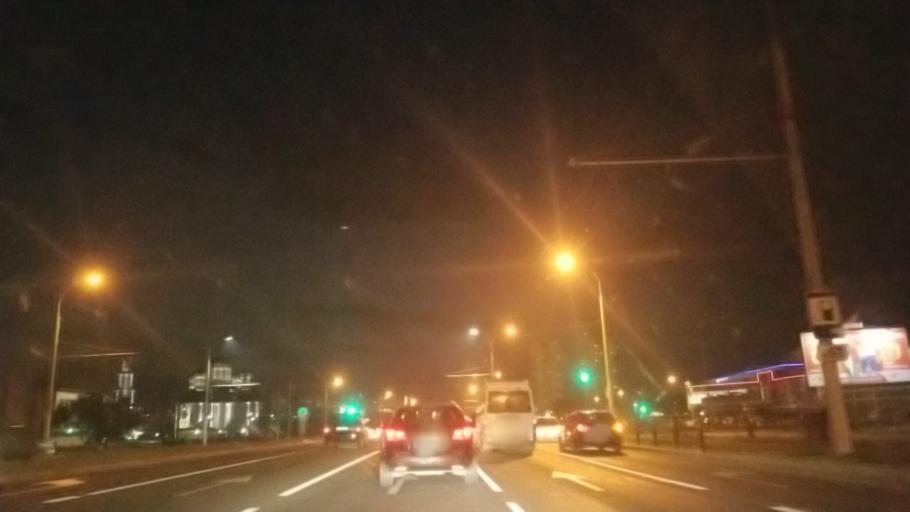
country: BY
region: Brest
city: Brest
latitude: 52.0955
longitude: 23.7663
